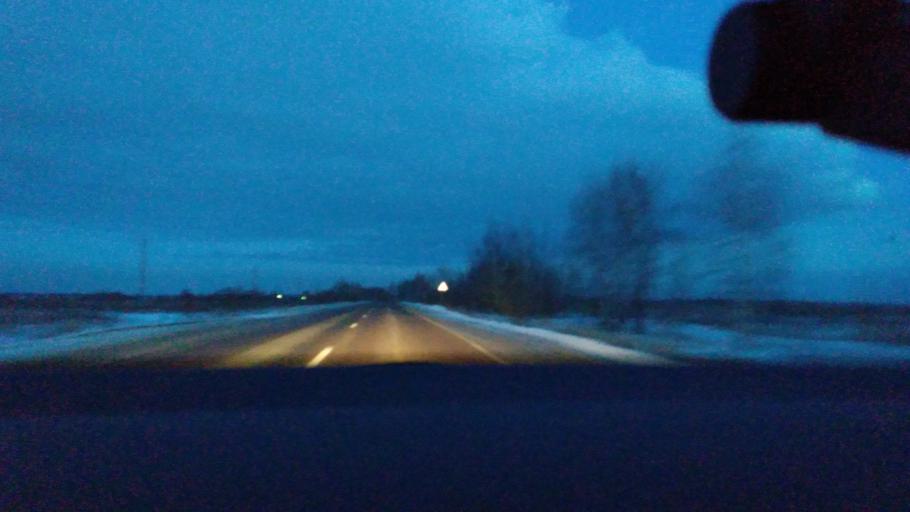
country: RU
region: Moskovskaya
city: Krasnaya Poyma
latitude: 55.1674
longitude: 39.1666
